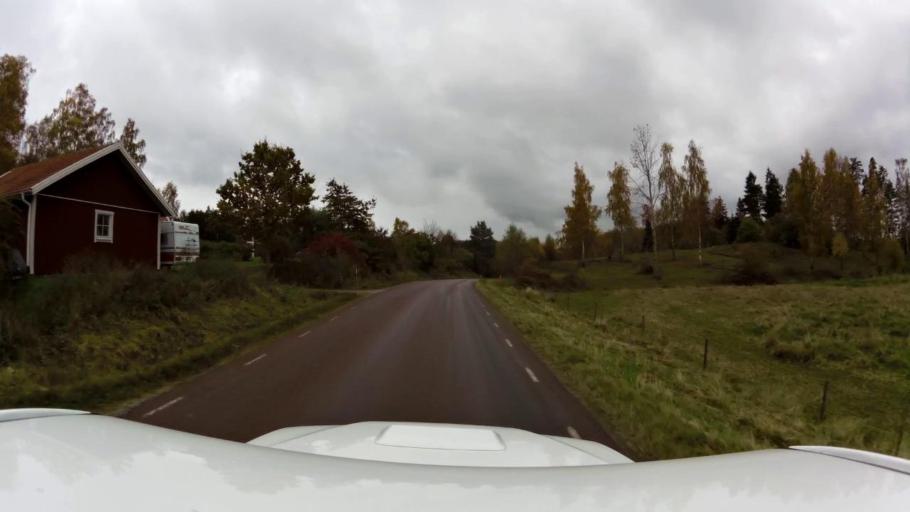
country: SE
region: OEstergoetland
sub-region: Linkopings Kommun
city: Ljungsbro
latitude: 58.5666
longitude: 15.5154
